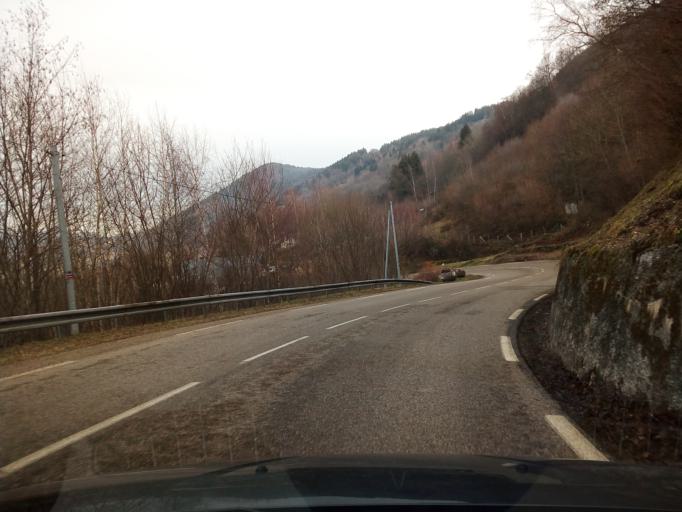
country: FR
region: Rhone-Alpes
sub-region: Departement de l'Isere
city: Revel
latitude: 45.1412
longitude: 5.8546
